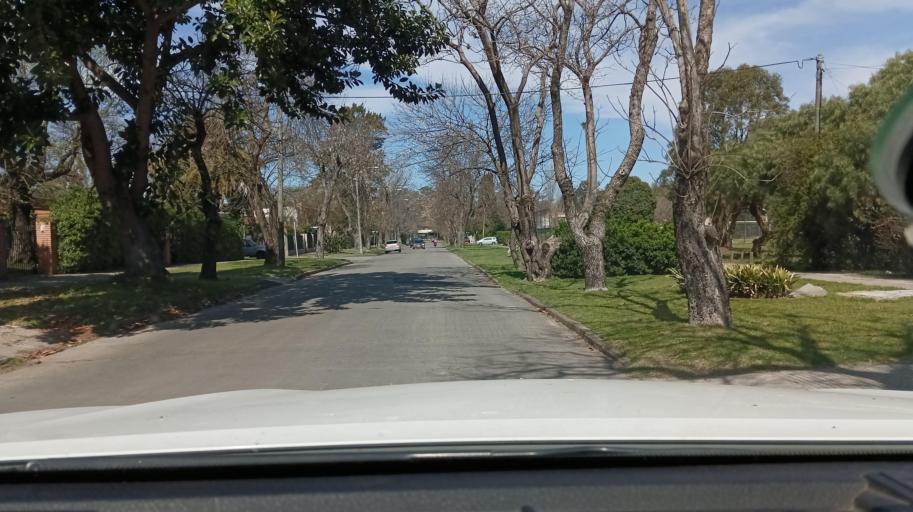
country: UY
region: Canelones
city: Paso de Carrasco
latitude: -34.8840
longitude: -56.0651
